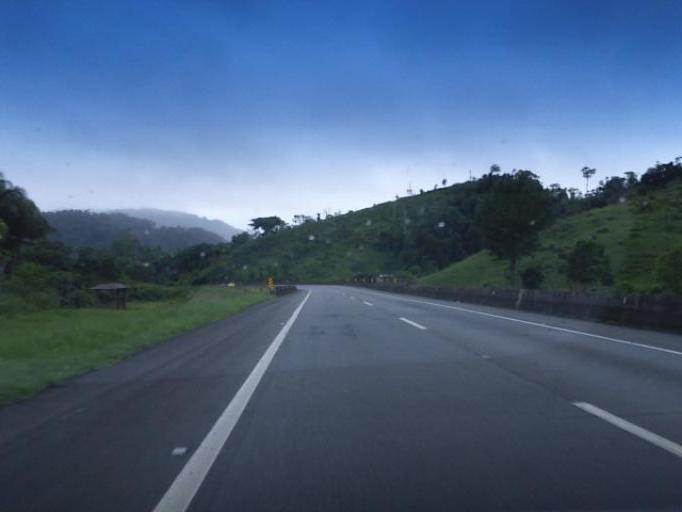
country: BR
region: Parana
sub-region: Antonina
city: Antonina
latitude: -25.0409
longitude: -48.5382
